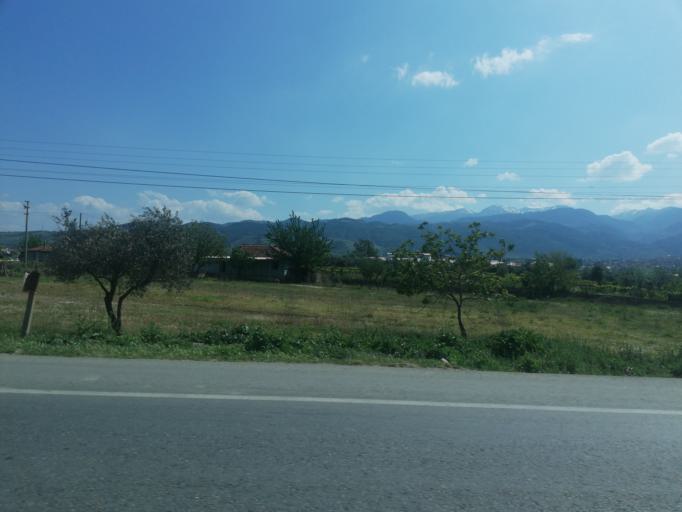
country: TR
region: Manisa
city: Alasehir
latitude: 38.3594
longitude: 28.5355
